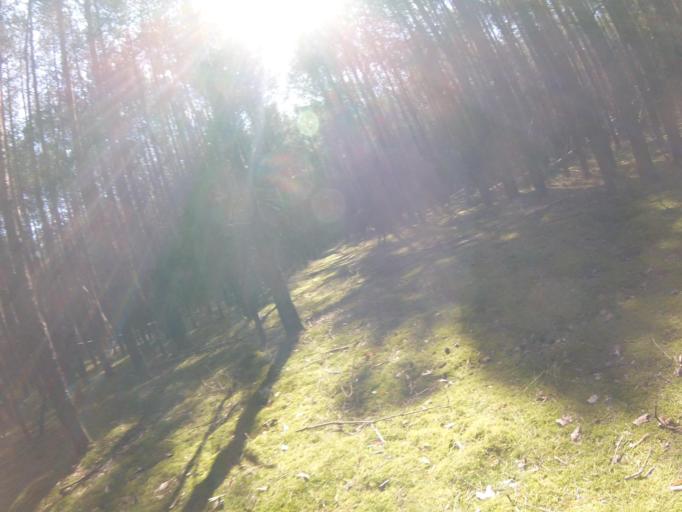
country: DE
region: Brandenburg
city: Bestensee
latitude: 52.2624
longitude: 13.6838
